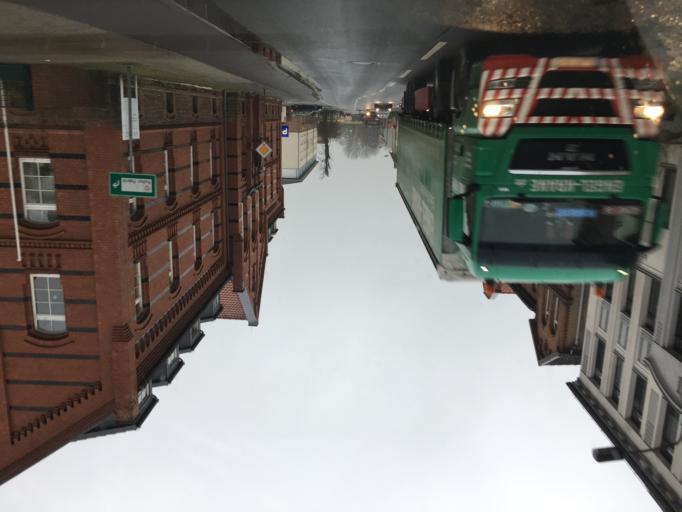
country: DE
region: Saxony-Anhalt
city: Haldensleben I
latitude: 52.2866
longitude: 11.4087
